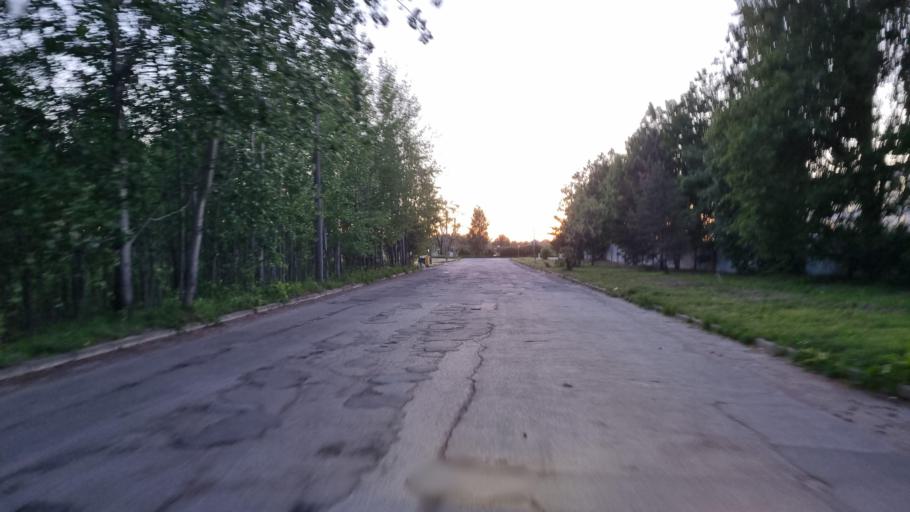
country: LV
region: Riga
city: Daugavgriva
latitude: 57.0240
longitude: 24.0272
